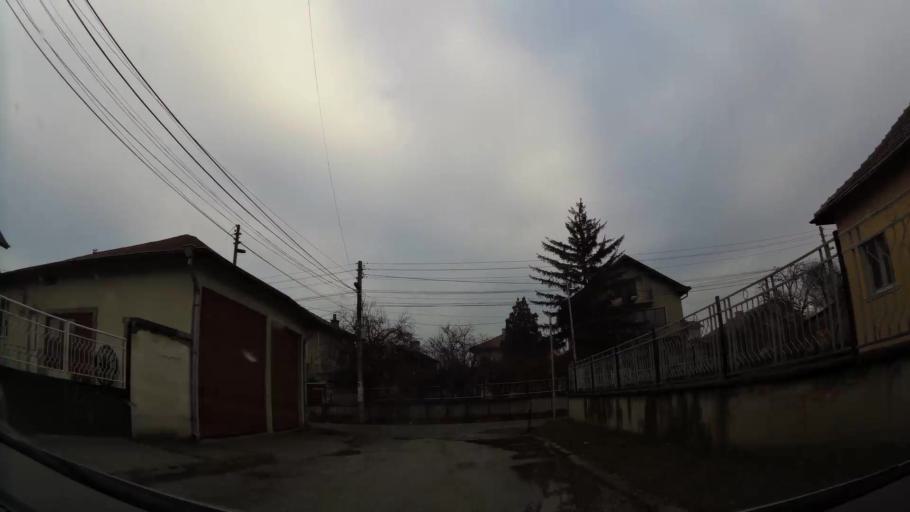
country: BG
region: Sofia-Capital
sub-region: Stolichna Obshtina
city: Sofia
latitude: 42.7463
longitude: 23.3474
